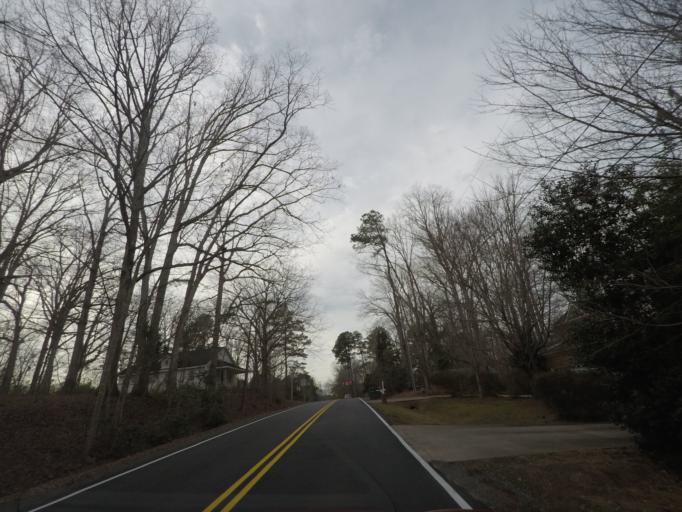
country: US
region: North Carolina
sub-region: Durham County
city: Durham
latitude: 36.0427
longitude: -78.9559
